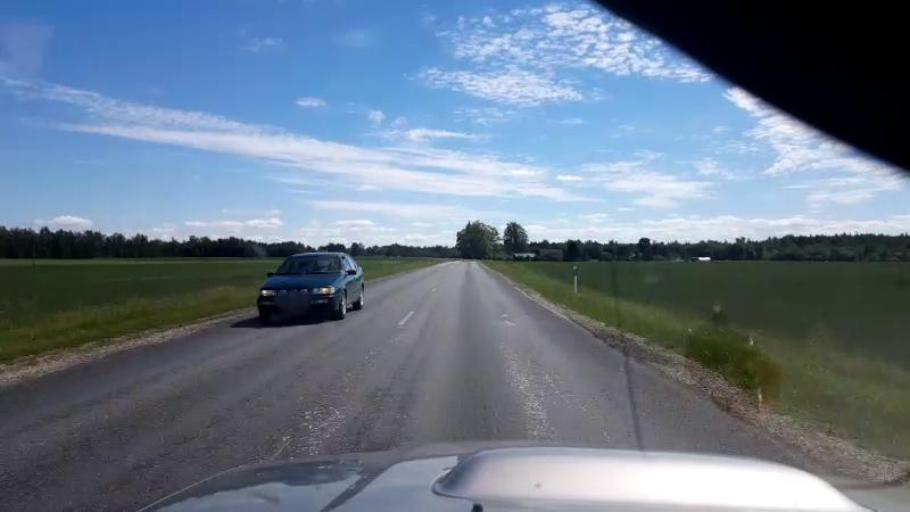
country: EE
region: Laeaene-Virumaa
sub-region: Rakke vald
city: Rakke
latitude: 58.8917
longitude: 26.2854
